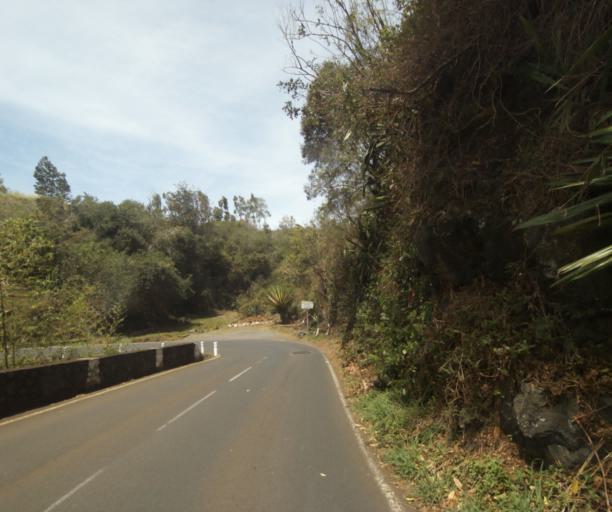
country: RE
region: Reunion
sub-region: Reunion
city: Saint-Paul
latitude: -21.0446
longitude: 55.2892
